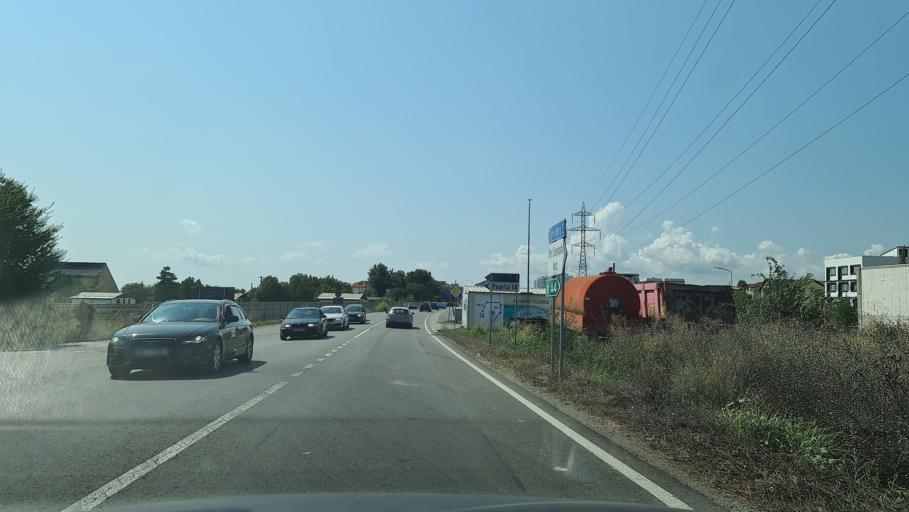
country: RO
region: Constanta
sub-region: Oras Eforie
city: Eforie Nord
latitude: 44.0853
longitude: 28.6398
